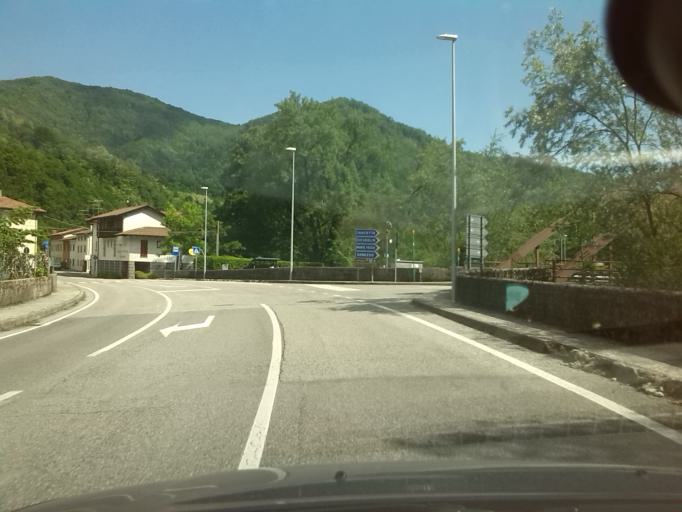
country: IT
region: Friuli Venezia Giulia
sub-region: Provincia di Udine
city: Pulfero
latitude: 46.1735
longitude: 13.4827
